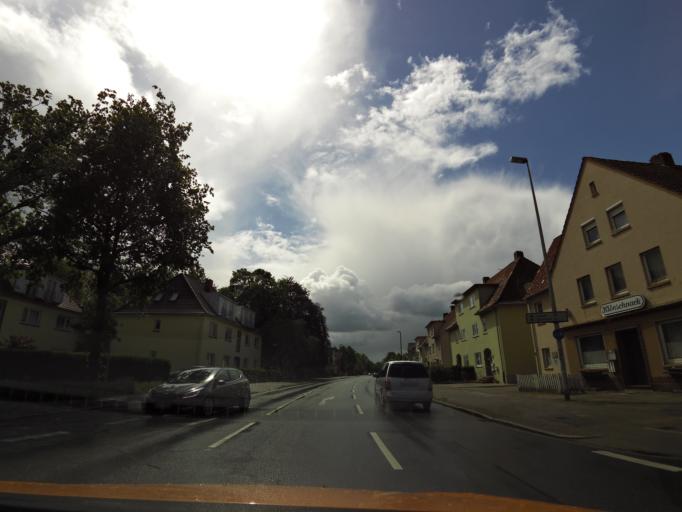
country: DE
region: Lower Saxony
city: Delmenhorst
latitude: 53.0426
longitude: 8.6378
